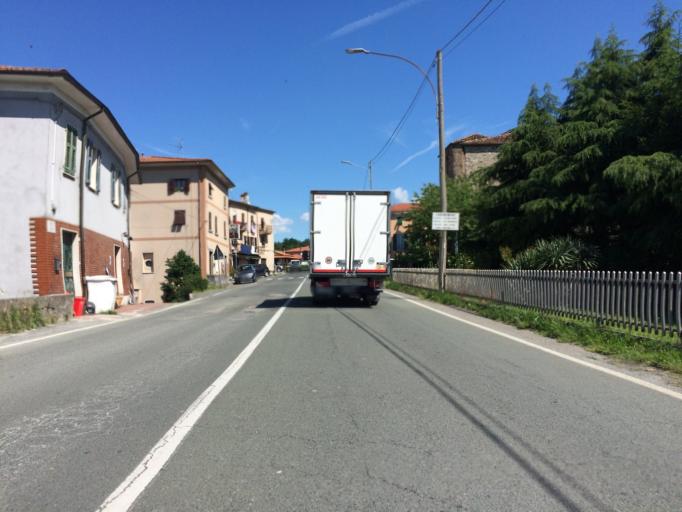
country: IT
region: Tuscany
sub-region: Provincia di Massa-Carrara
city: Terrarossa
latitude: 44.2292
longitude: 9.9651
